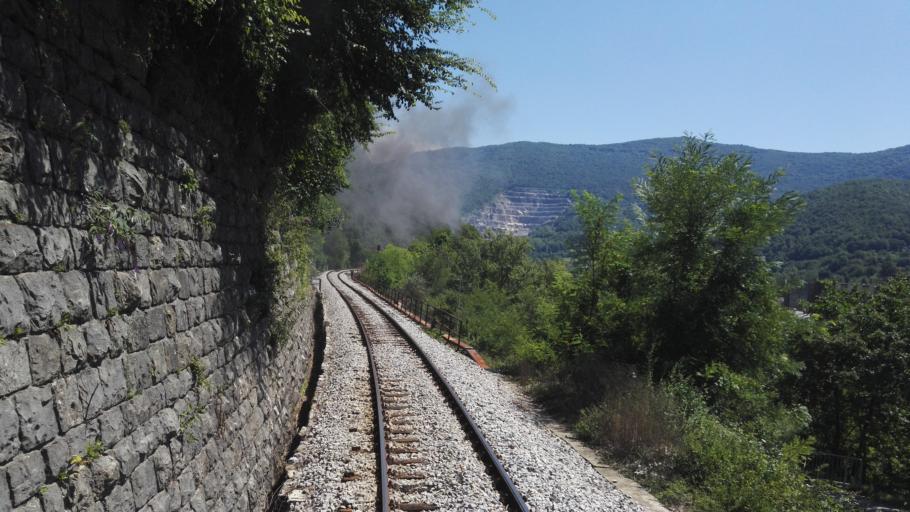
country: SI
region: Kanal
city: Deskle
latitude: 46.0540
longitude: 13.6091
